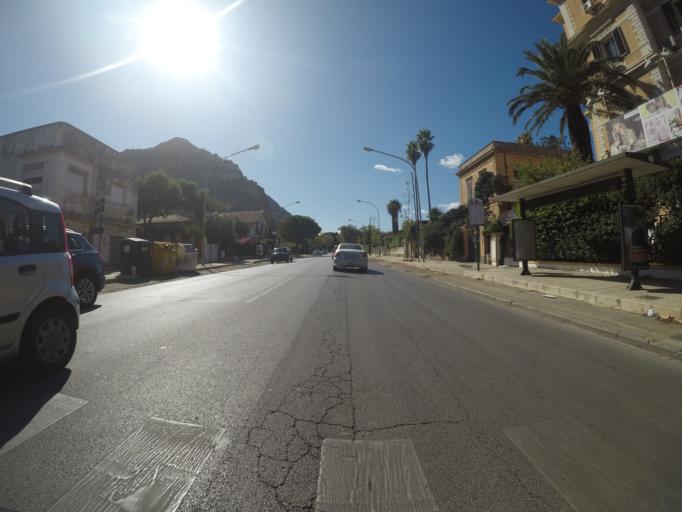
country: IT
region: Sicily
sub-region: Palermo
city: Palermo
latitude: 38.1934
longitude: 13.3323
